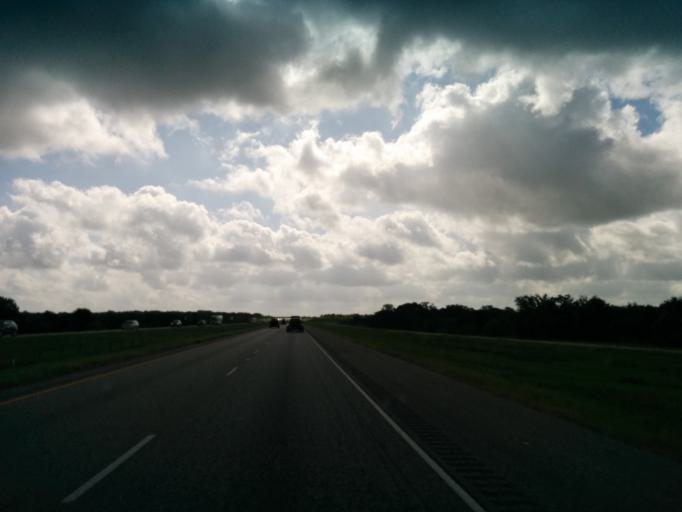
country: US
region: Texas
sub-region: Gonzales County
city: Waelder
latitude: 29.6632
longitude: -97.3731
